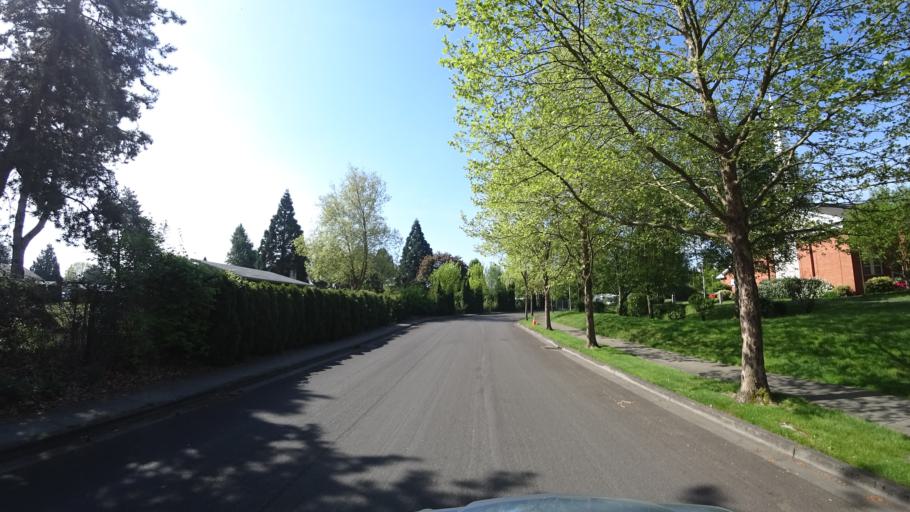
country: US
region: Oregon
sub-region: Washington County
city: Hillsboro
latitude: 45.5237
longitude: -122.9493
